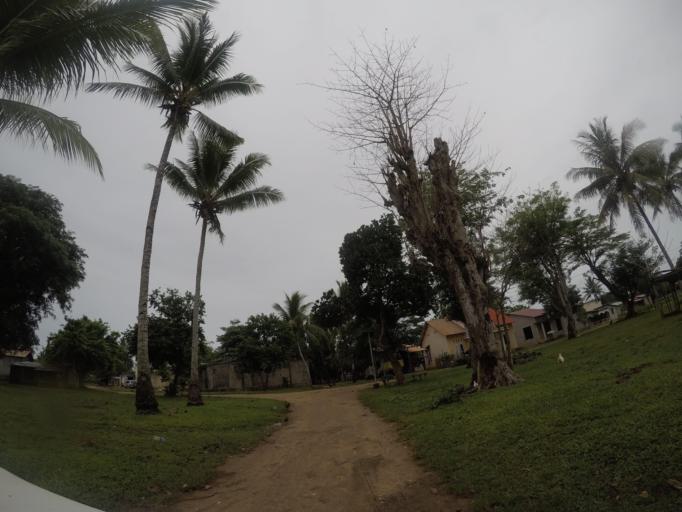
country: TL
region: Lautem
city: Lospalos
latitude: -8.5208
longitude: 127.0052
